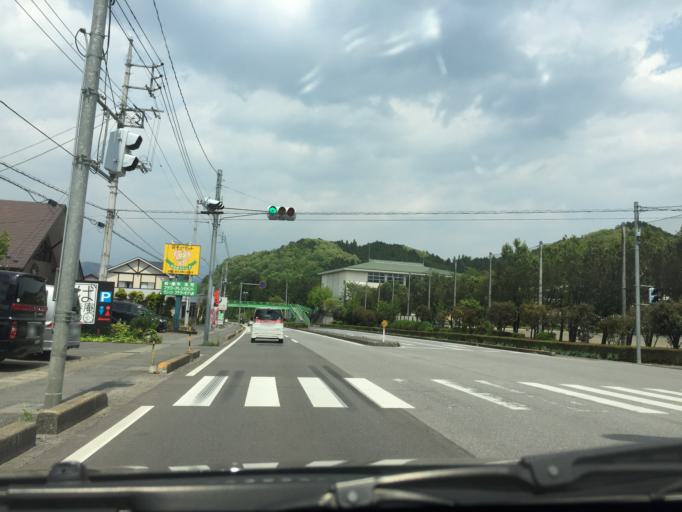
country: JP
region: Tochigi
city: Imaichi
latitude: 36.7489
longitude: 139.7135
